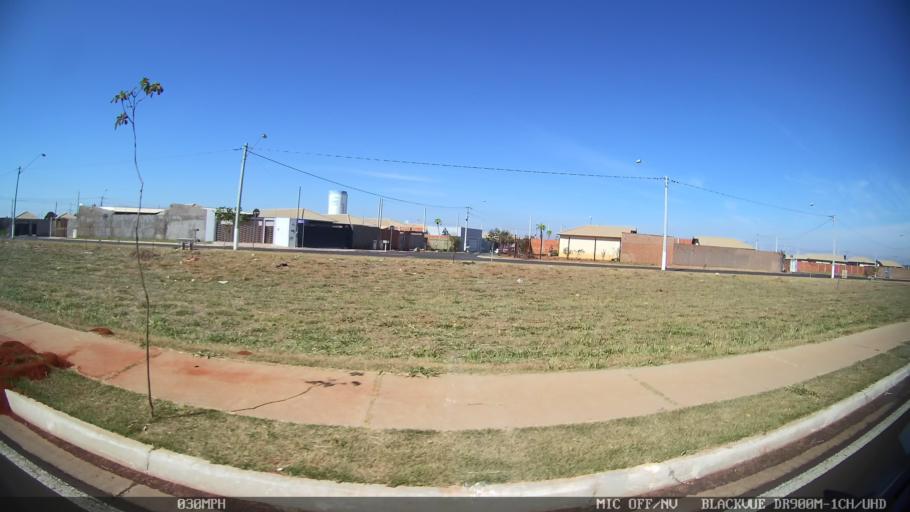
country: BR
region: Sao Paulo
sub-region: Sao Jose Do Rio Preto
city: Sao Jose do Rio Preto
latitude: -20.7476
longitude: -49.4372
